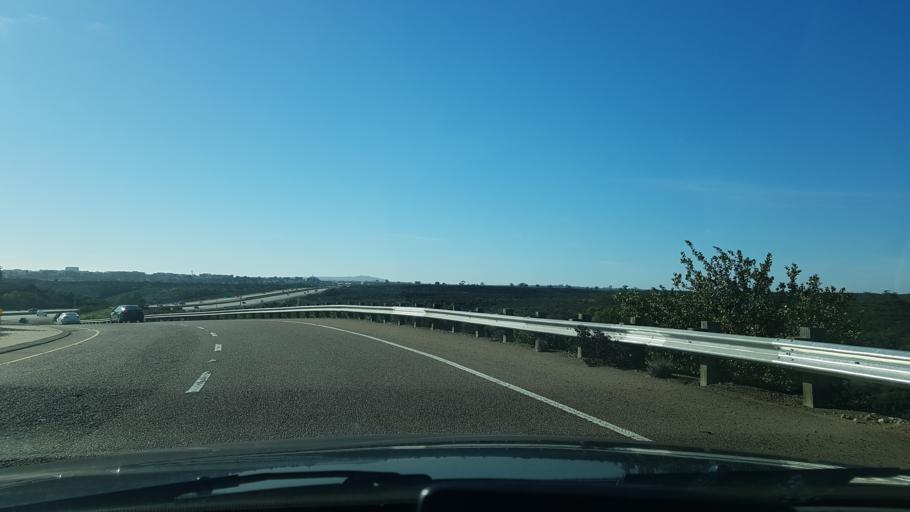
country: US
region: California
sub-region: San Diego County
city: La Mesa
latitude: 32.8428
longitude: -117.0976
